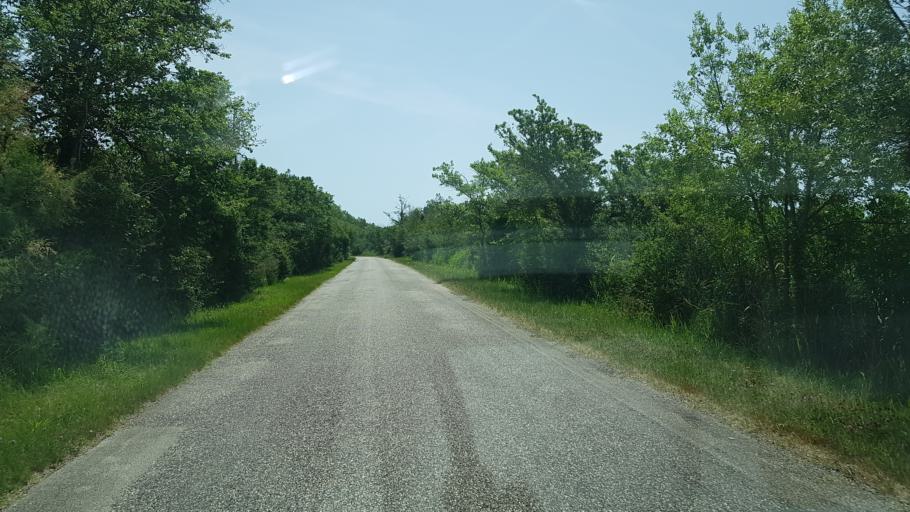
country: FR
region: Provence-Alpes-Cote d'Azur
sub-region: Departement des Bouches-du-Rhone
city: Port-Saint-Louis-du-Rhone
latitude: 43.4594
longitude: 4.6584
